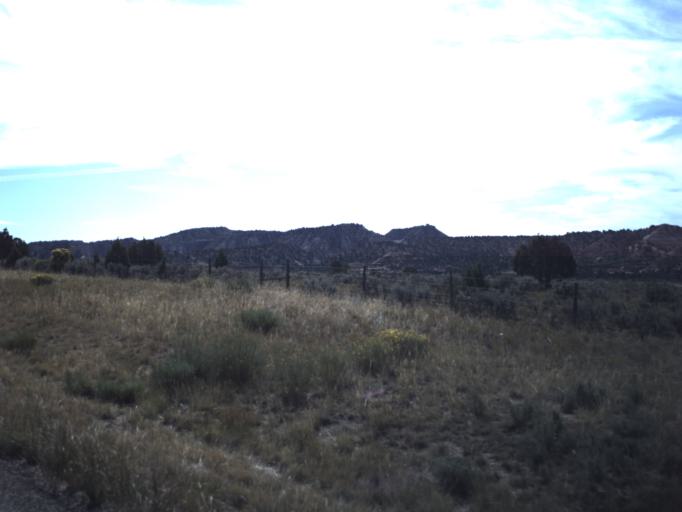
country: US
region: Utah
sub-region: Garfield County
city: Panguitch
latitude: 37.5594
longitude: -112.0224
